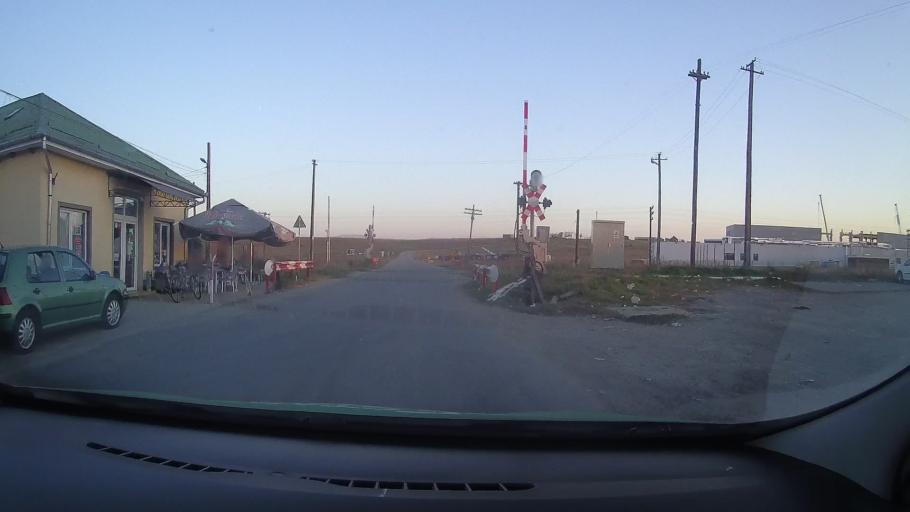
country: RO
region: Timis
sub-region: Comuna Manastiur
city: Manastiur
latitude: 45.8281
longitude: 22.0689
